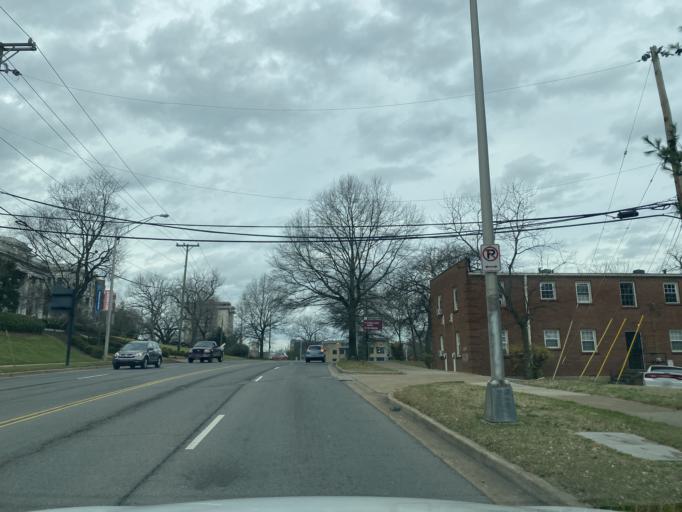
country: US
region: Tennessee
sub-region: Davidson County
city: Nashville
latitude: 36.1362
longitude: -86.7936
